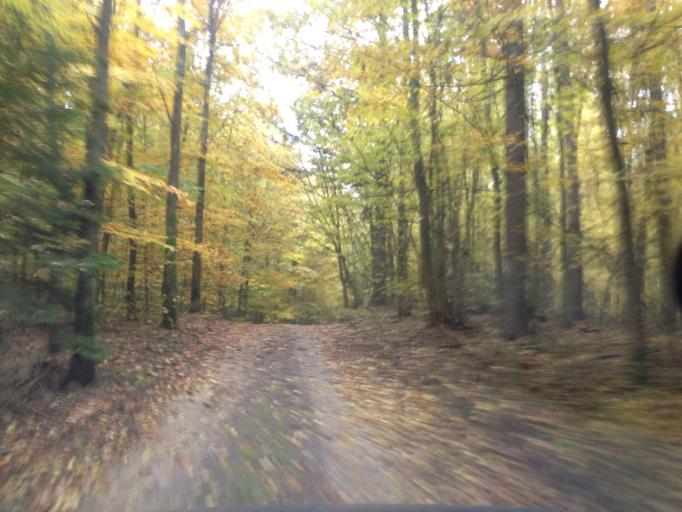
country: PL
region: Kujawsko-Pomorskie
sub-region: Powiat brodnicki
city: Gorzno
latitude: 53.2242
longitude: 19.7155
